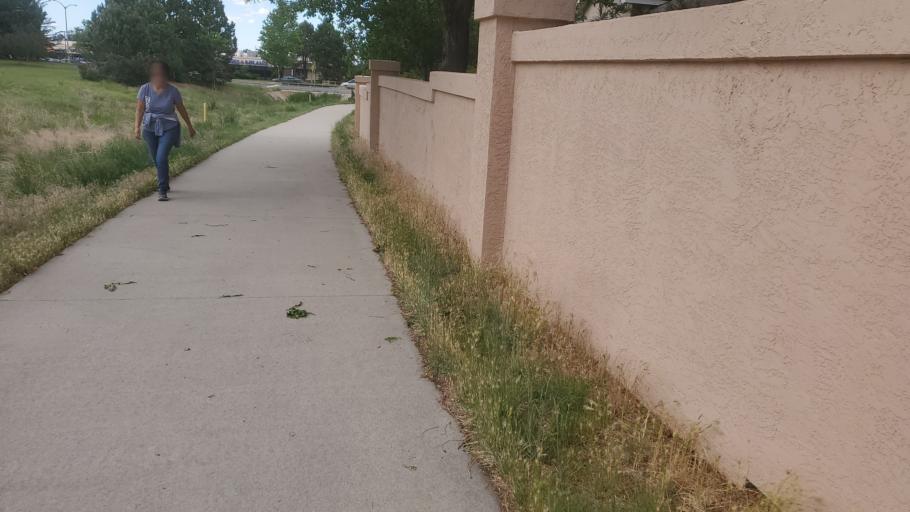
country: US
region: Colorado
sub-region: Adams County
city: Aurora
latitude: 39.6738
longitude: -104.8442
